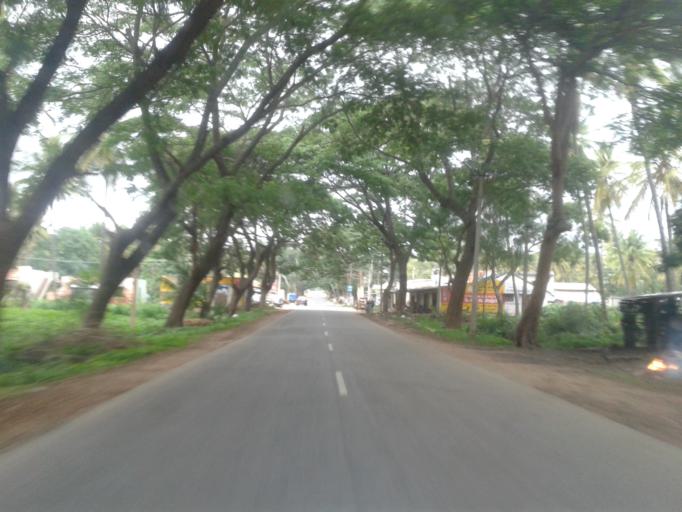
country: IN
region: Karnataka
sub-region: Hassan
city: Shravanabelagola
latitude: 12.8710
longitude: 76.4518
